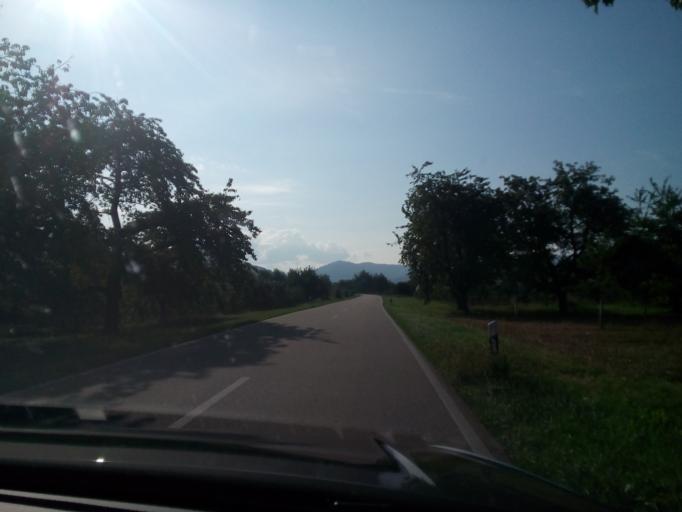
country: DE
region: Baden-Wuerttemberg
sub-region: Freiburg Region
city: Haslach
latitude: 48.5552
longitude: 8.0515
